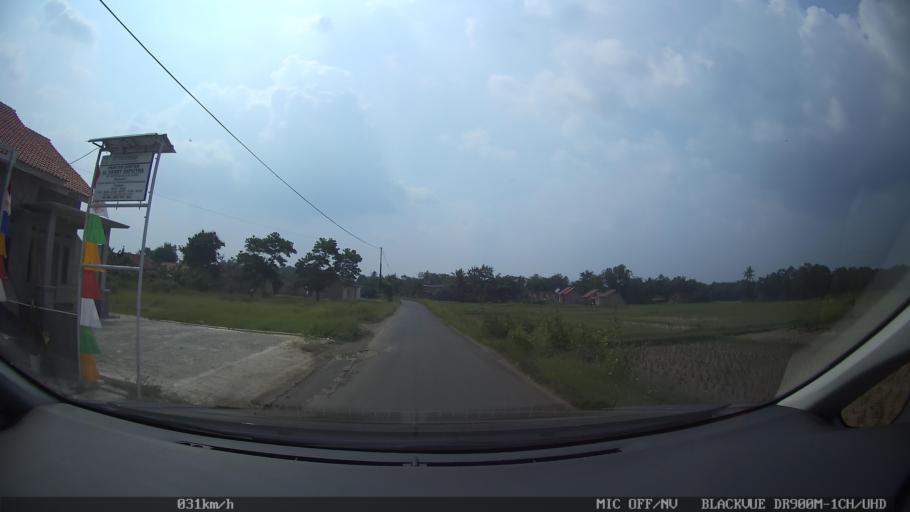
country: ID
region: Lampung
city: Gadingrejo
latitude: -5.3558
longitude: 105.0381
